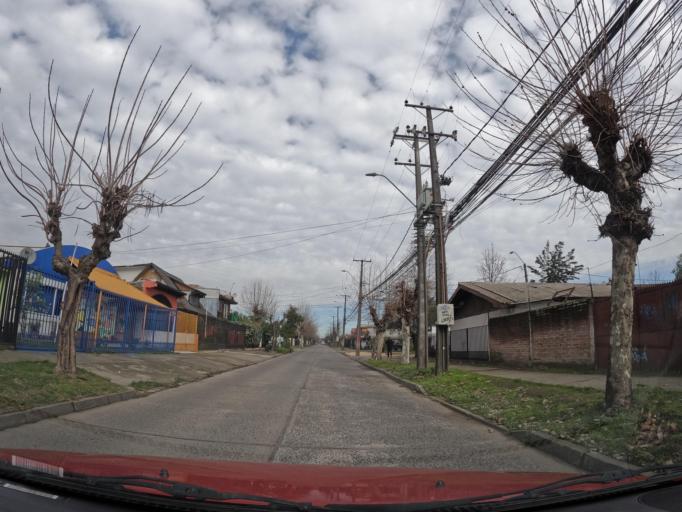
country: CL
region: Maule
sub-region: Provincia de Linares
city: Linares
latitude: -35.8405
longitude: -71.6034
